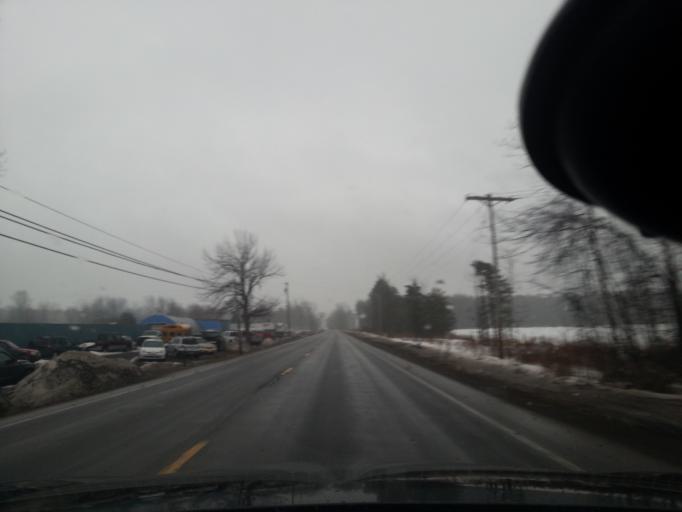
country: US
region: New York
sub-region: St. Lawrence County
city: Ogdensburg
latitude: 44.6503
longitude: -75.4429
